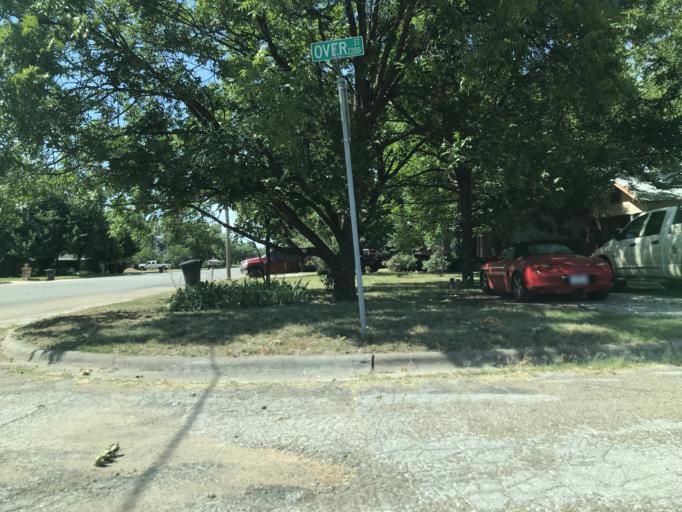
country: US
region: Texas
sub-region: Taylor County
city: Abilene
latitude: 32.4239
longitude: -99.7494
